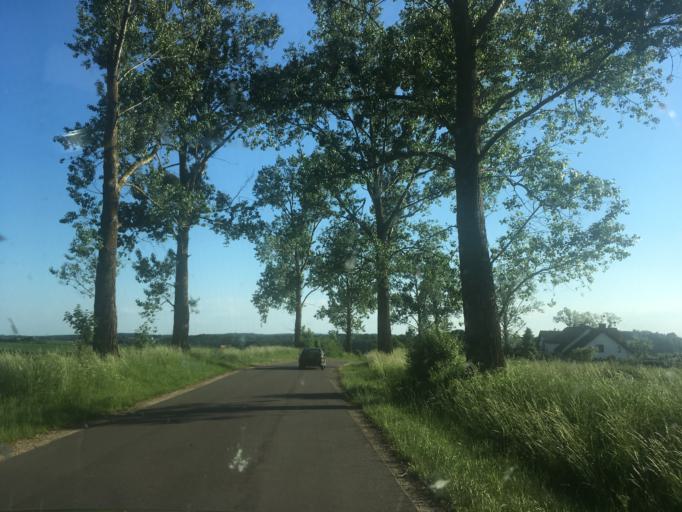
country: PL
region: Warmian-Masurian Voivodeship
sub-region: Powiat ostrodzki
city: Ostroda
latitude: 53.6743
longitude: 20.0393
